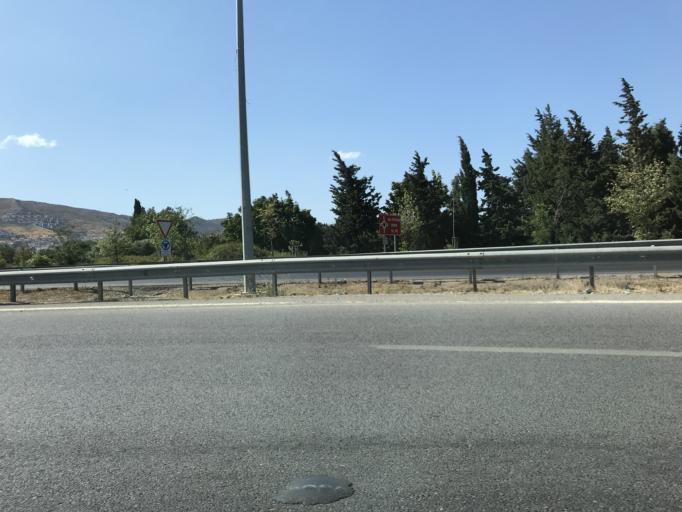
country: TR
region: Izmir
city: Urla
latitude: 38.3650
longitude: 26.8723
